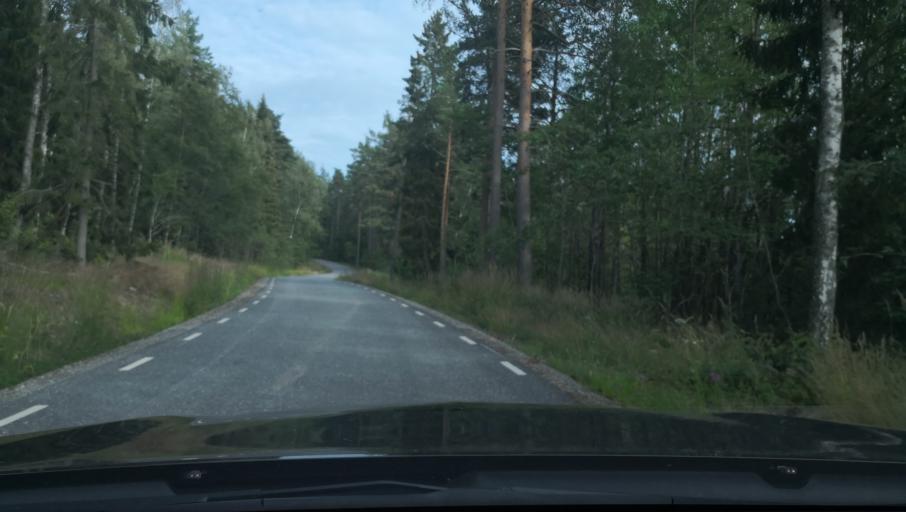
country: SE
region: Vaestmanland
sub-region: Hallstahammars Kommun
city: Hallstahammar
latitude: 59.6574
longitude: 16.1794
